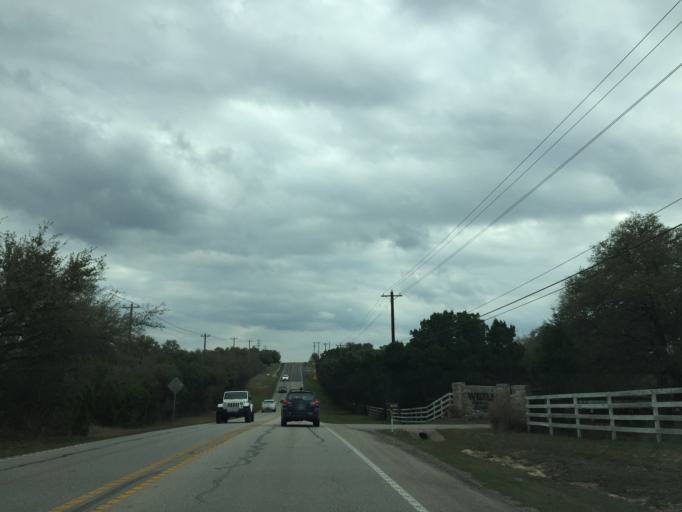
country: US
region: Texas
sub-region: Travis County
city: Shady Hollow
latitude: 30.1840
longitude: -97.9289
